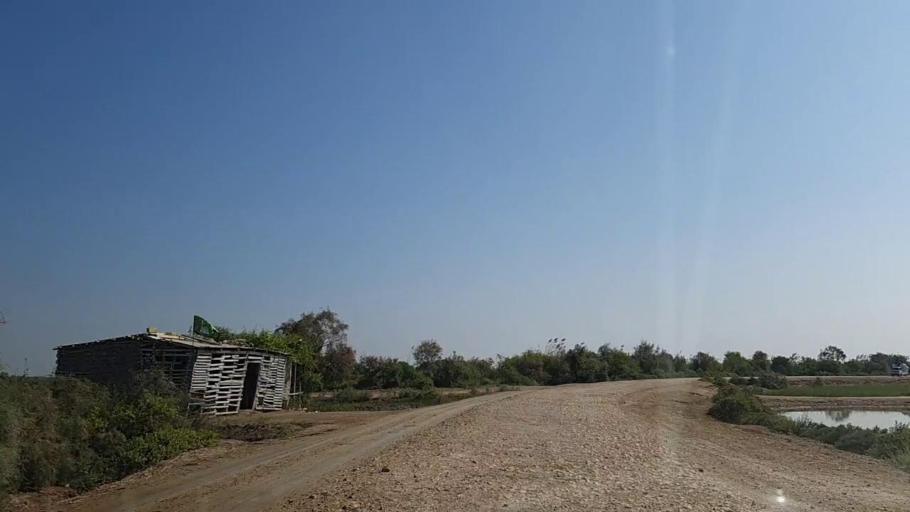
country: PK
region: Sindh
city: Chuhar Jamali
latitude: 24.4613
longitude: 68.1127
